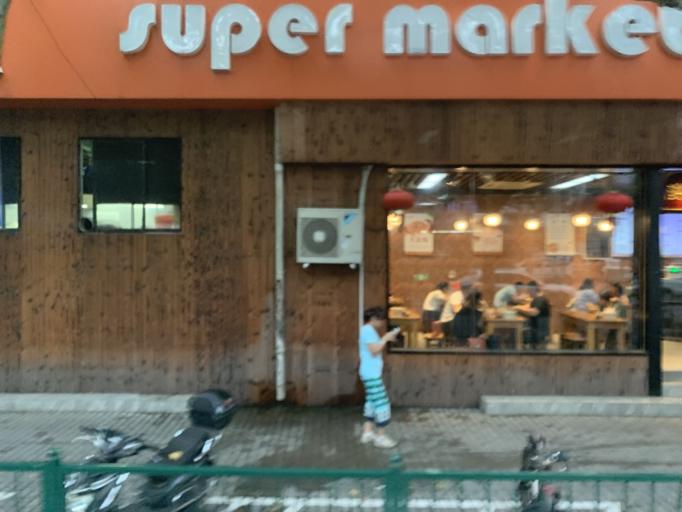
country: CN
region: Shanghai Shi
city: Pudong
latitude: 31.2452
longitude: 121.5394
